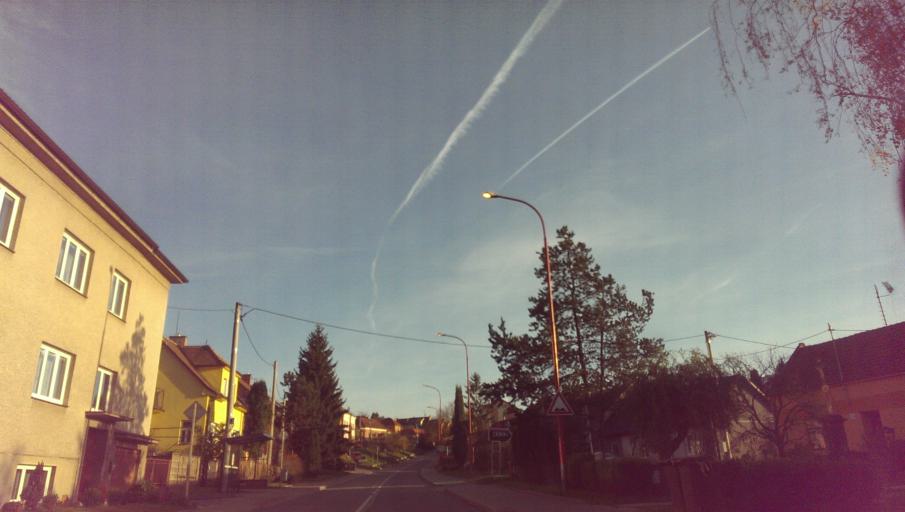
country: CZ
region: Zlin
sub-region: Okres Uherske Hradiste
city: Uherske Hradiste
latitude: 49.0681
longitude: 17.4773
